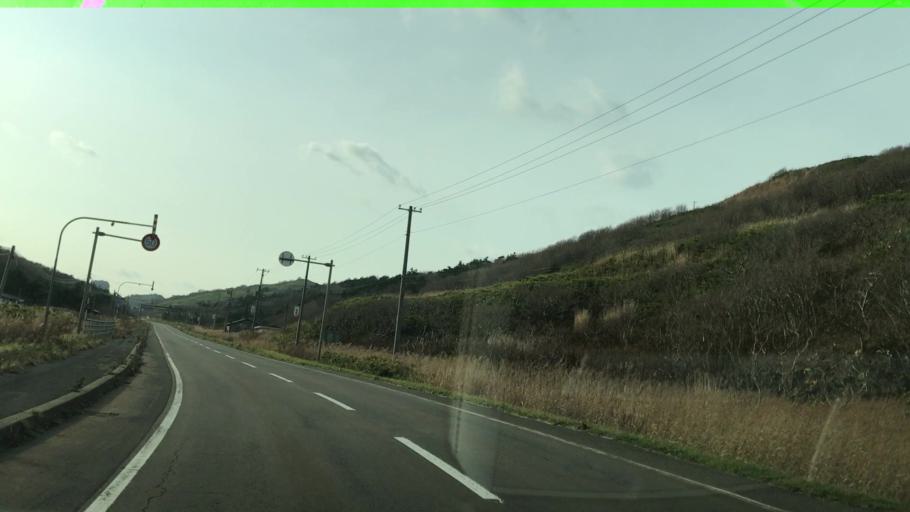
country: JP
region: Hokkaido
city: Iwanai
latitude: 43.3286
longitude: 140.3656
